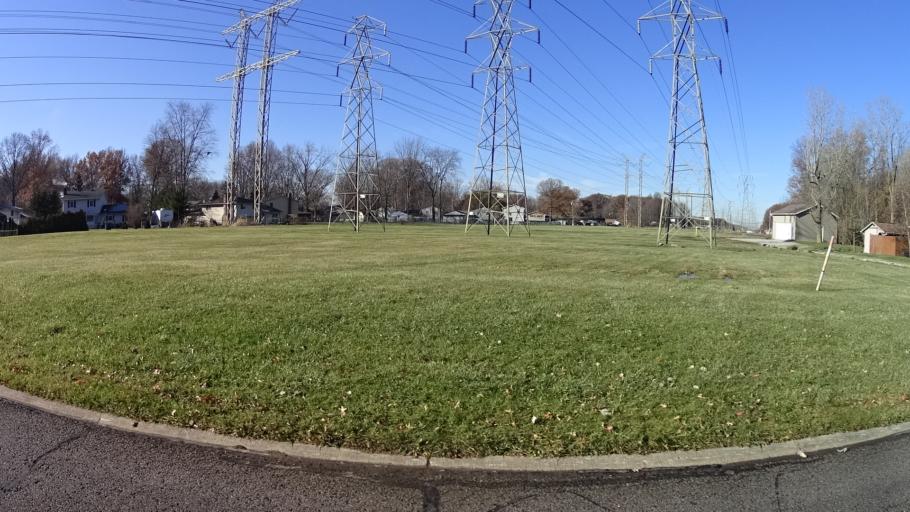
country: US
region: Ohio
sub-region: Lorain County
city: North Ridgeville
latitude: 41.4050
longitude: -81.9948
